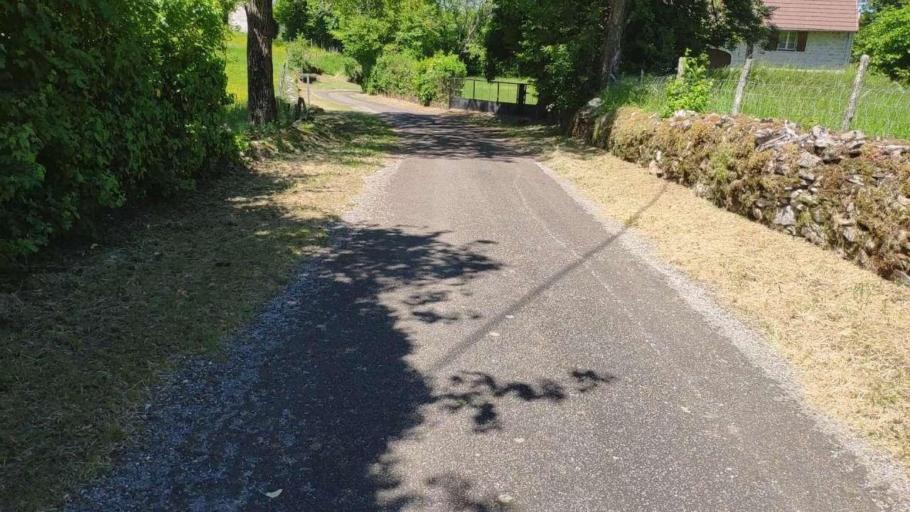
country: FR
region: Franche-Comte
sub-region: Departement du Jura
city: Poligny
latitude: 46.7441
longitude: 5.6730
